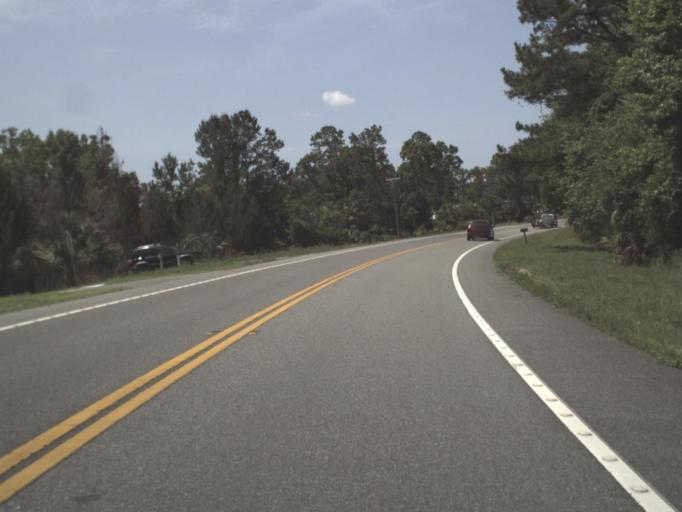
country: US
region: Florida
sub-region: Taylor County
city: Steinhatchee
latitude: 29.6910
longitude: -83.3562
